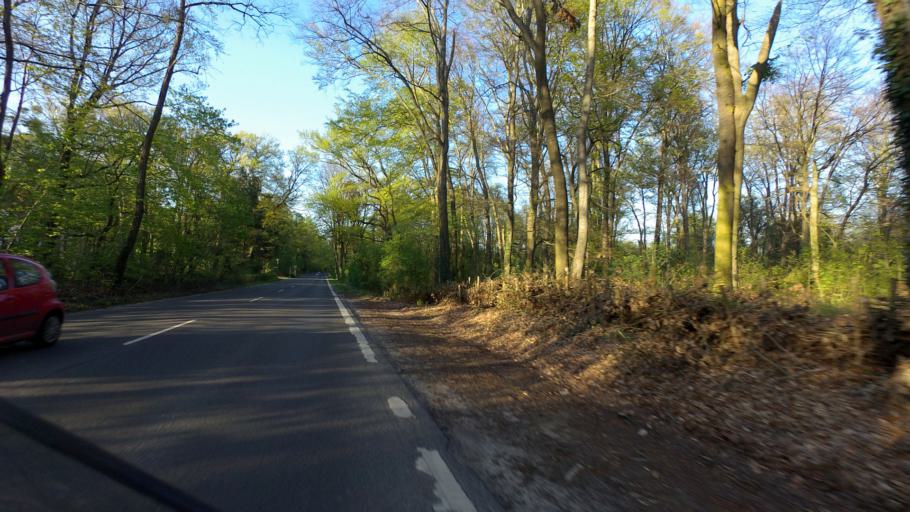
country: DE
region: Berlin
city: Kladow
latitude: 52.4745
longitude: 13.1123
